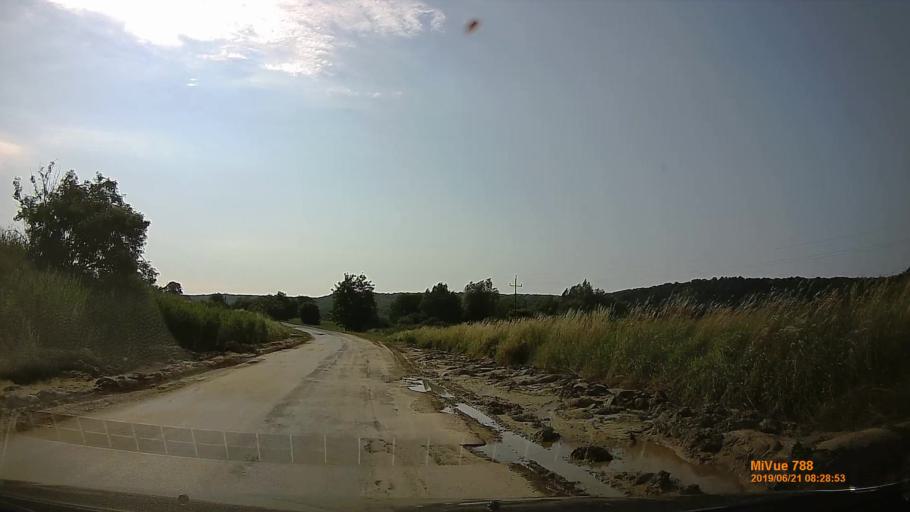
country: HU
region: Baranya
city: Szigetvar
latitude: 46.1456
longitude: 17.8374
